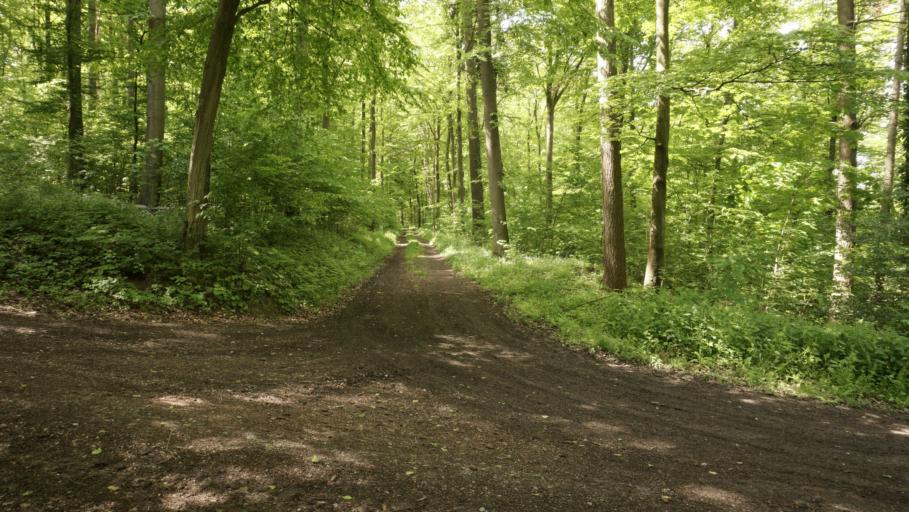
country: DE
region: Baden-Wuerttemberg
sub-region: Karlsruhe Region
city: Mosbach
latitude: 49.3708
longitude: 9.1622
